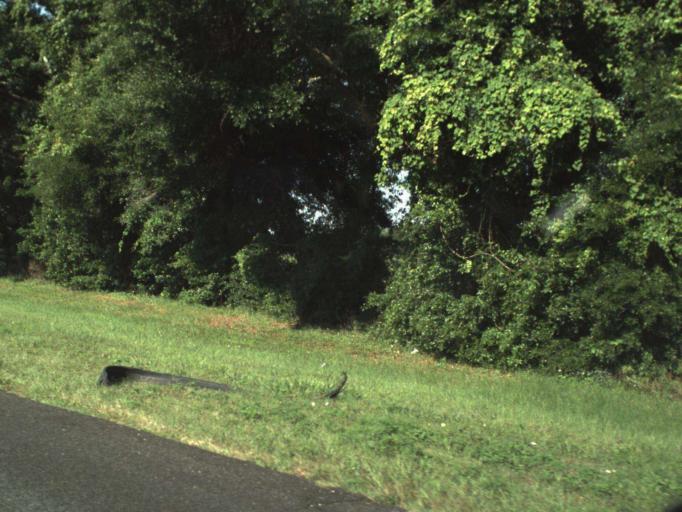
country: US
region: Florida
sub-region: Marion County
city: Citra
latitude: 29.3627
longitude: -82.1386
